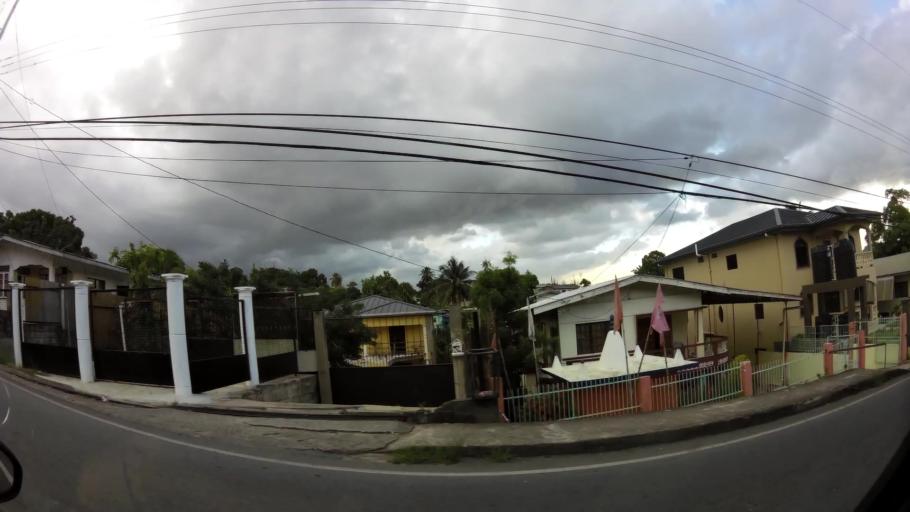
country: TT
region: City of San Fernando
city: Mon Repos
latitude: 10.2506
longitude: -61.4372
